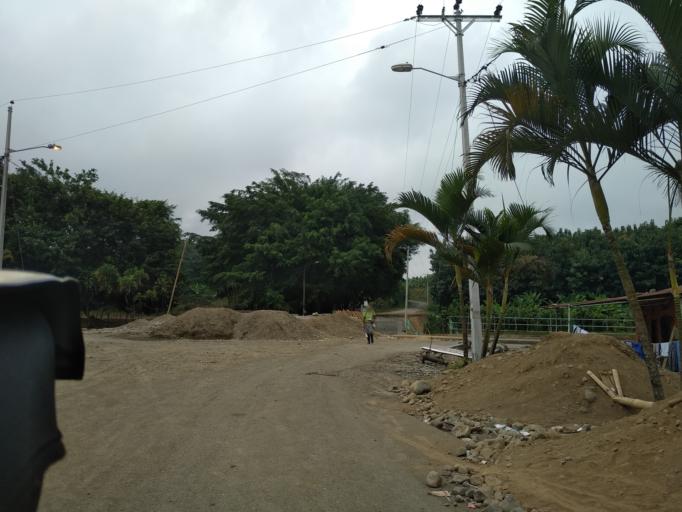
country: EC
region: Los Rios
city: Quevedo
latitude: -0.9803
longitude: -79.3521
